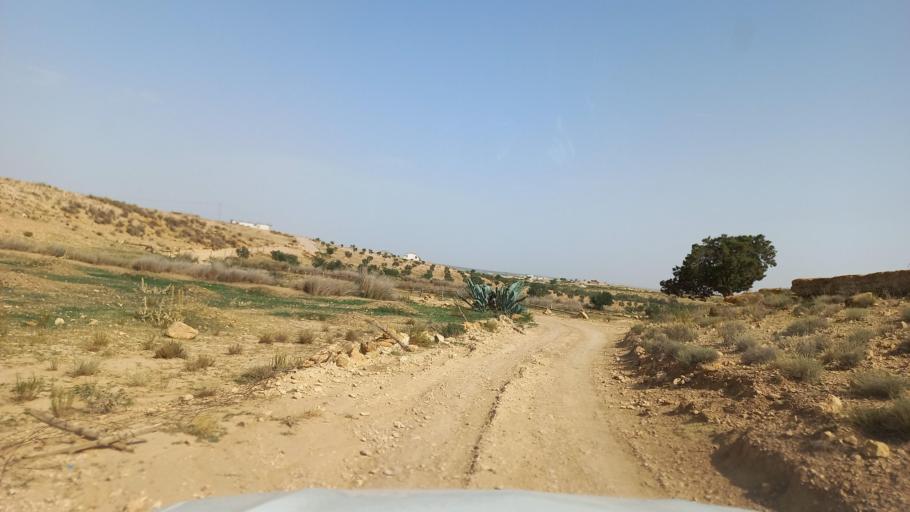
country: TN
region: Al Qasrayn
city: Kasserine
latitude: 35.3037
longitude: 8.9406
